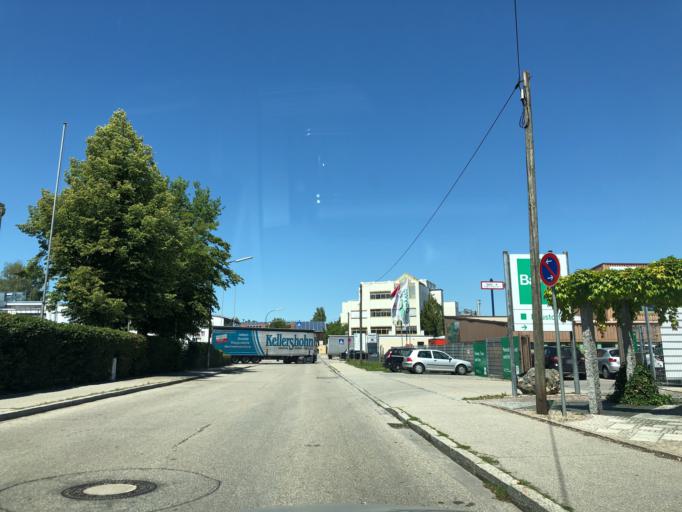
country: DE
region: Bavaria
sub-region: Upper Bavaria
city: Erding
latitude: 48.3135
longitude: 11.8899
